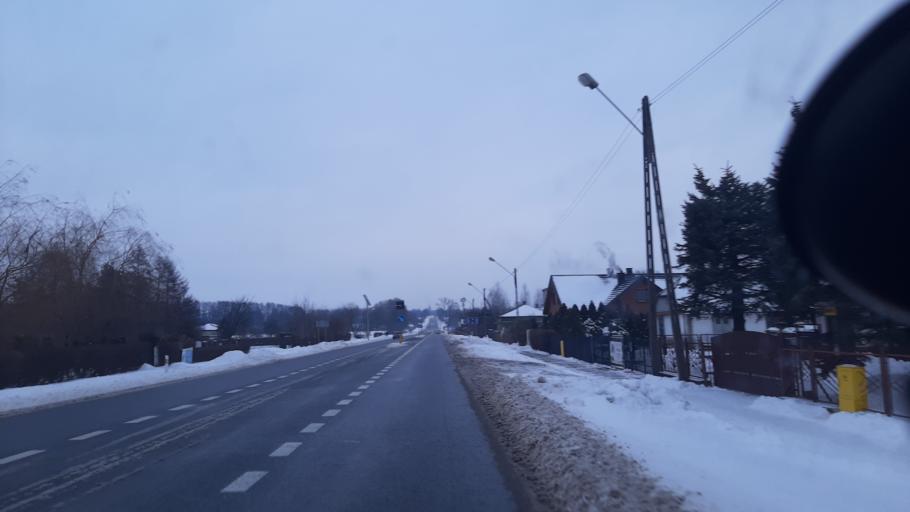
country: PL
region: Lublin Voivodeship
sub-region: Powiat lubelski
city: Garbow
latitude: 51.3632
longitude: 22.3016
